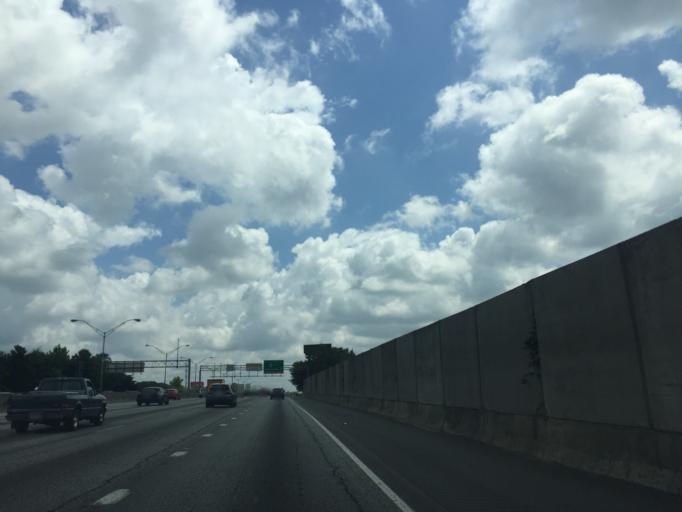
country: US
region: Georgia
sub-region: DeKalb County
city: Druid Hills
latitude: 33.8053
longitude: -84.3822
